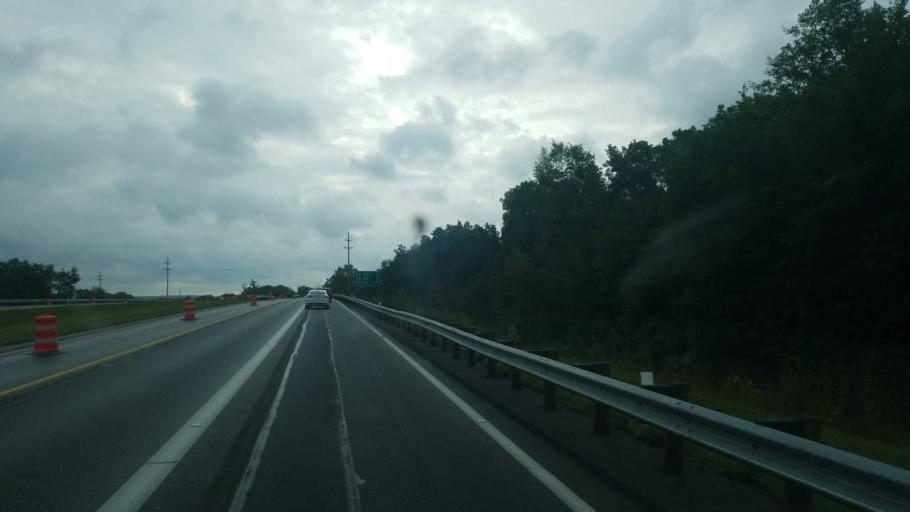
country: US
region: Ohio
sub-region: Cuyahoga County
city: Solon
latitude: 41.3924
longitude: -81.4241
